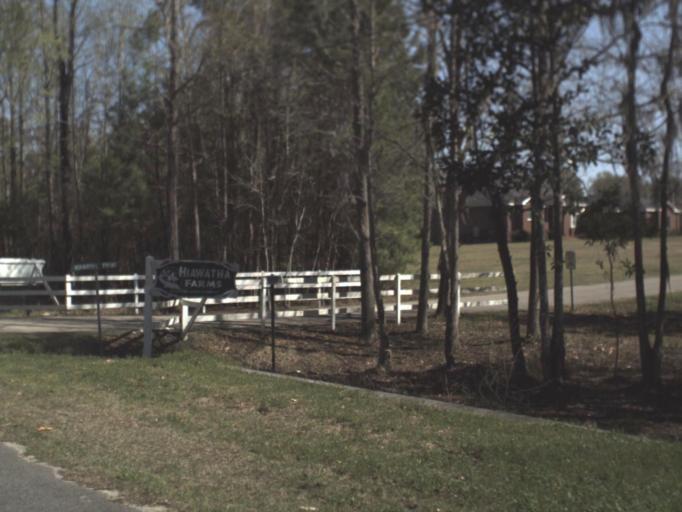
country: US
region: Florida
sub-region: Jefferson County
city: Monticello
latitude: 30.5049
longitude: -84.0242
